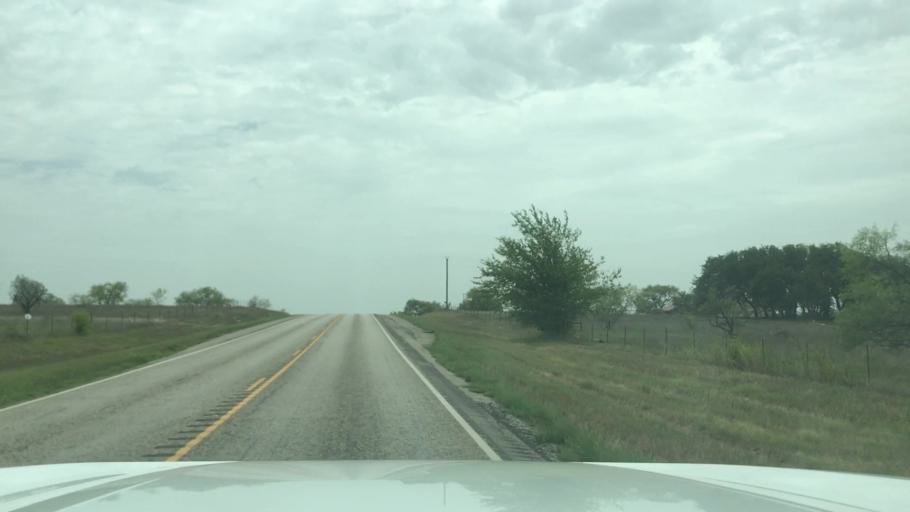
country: US
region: Texas
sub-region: Hamilton County
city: Hico
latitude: 32.0516
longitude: -98.1660
